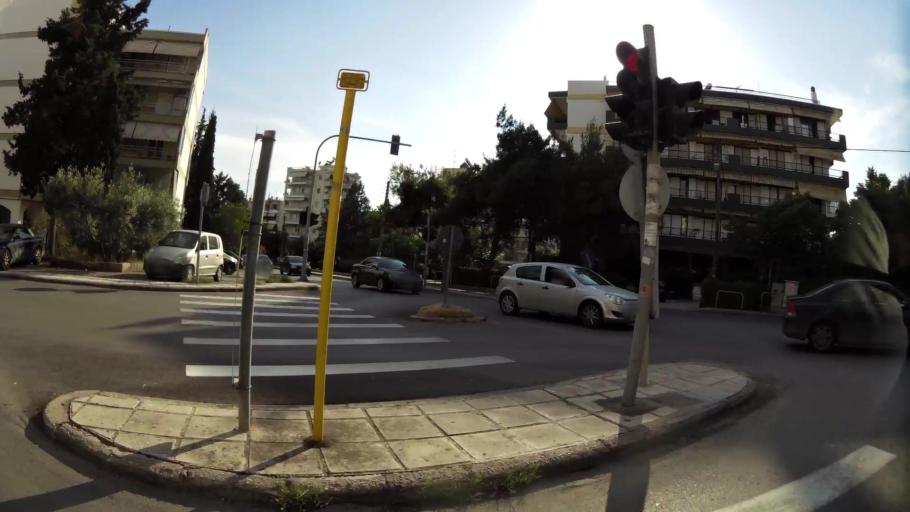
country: GR
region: Central Macedonia
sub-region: Nomos Thessalonikis
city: Kalamaria
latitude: 40.5741
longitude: 22.9628
